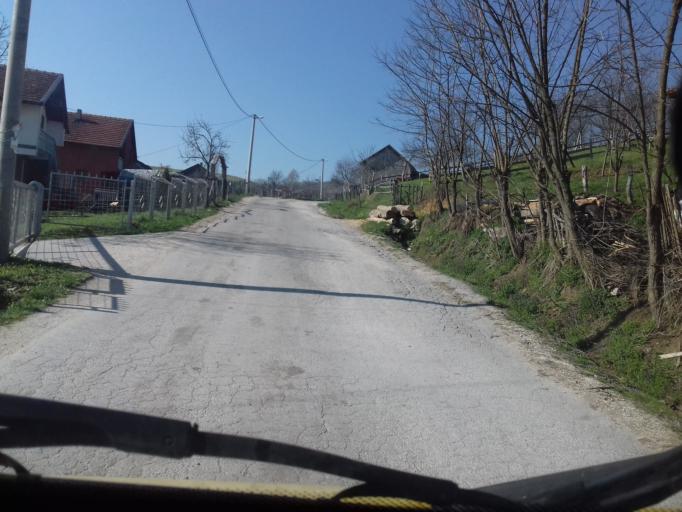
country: BA
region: Federation of Bosnia and Herzegovina
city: Travnik
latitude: 44.2515
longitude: 17.7454
